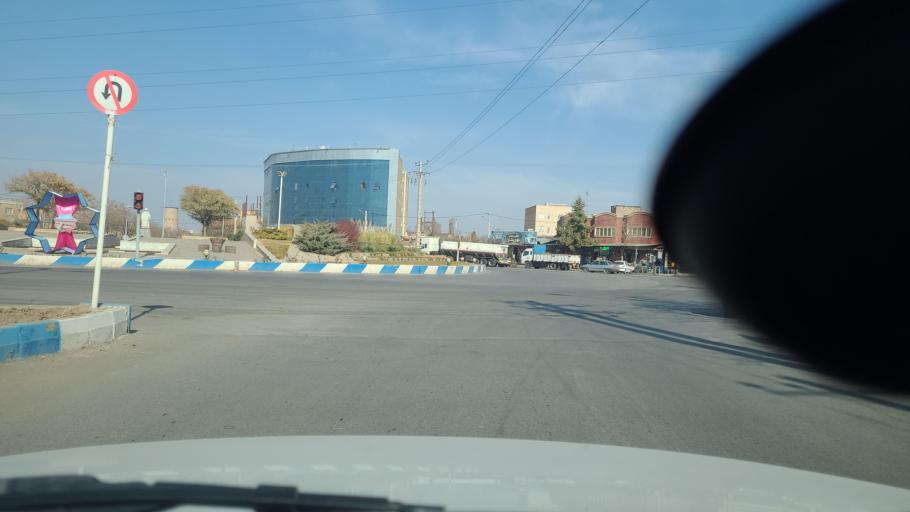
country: IR
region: Razavi Khorasan
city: Fariman
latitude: 35.6940
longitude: 59.8444
